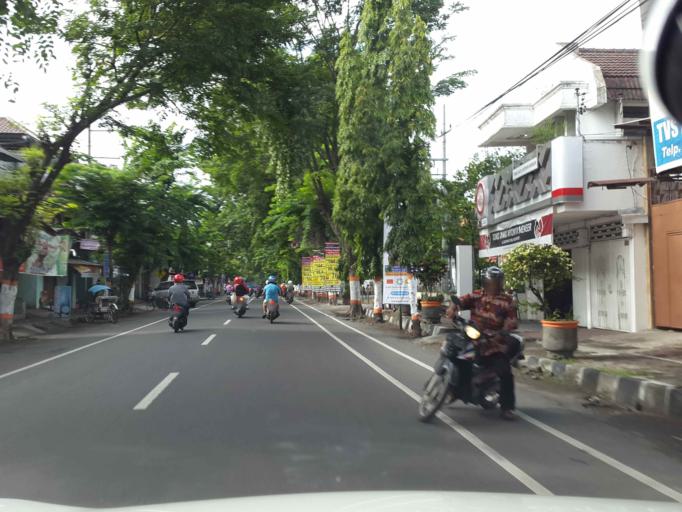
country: ID
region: East Java
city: Mojokerto
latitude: -7.4747
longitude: 112.4320
